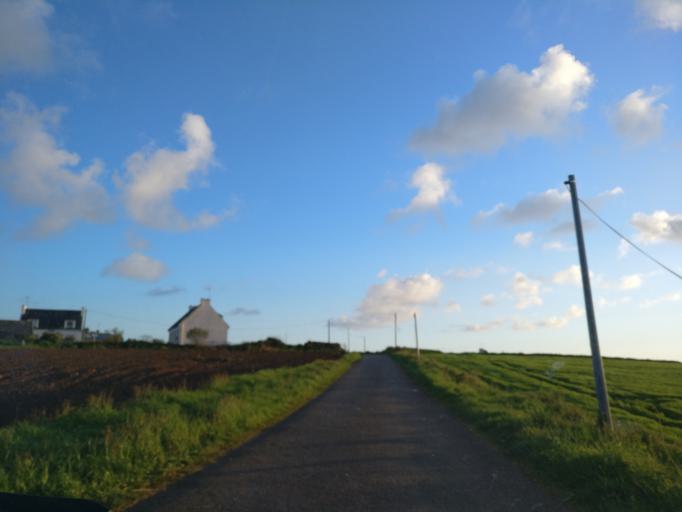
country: FR
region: Brittany
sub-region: Departement du Finistere
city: Lampaul-Plouarzel
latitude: 48.4582
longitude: -4.7540
